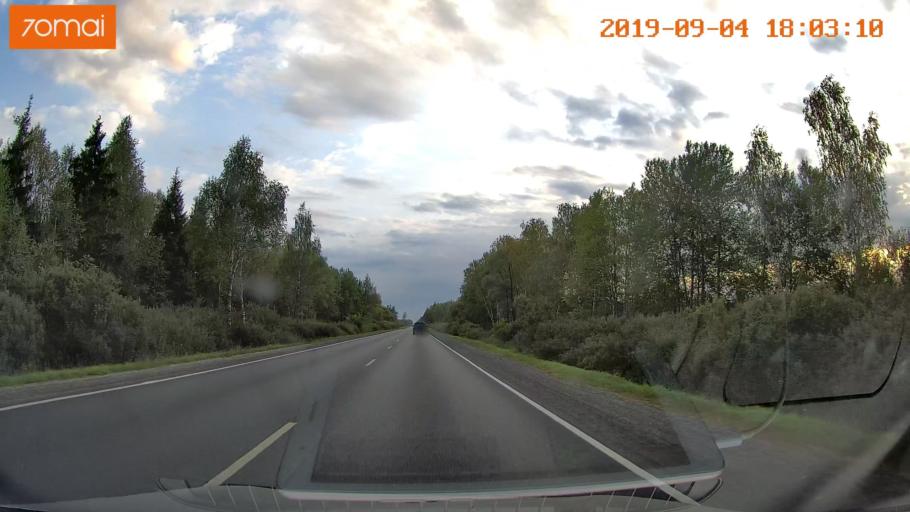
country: RU
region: Moskovskaya
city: Il'inskiy Pogost
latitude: 55.4664
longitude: 38.8556
